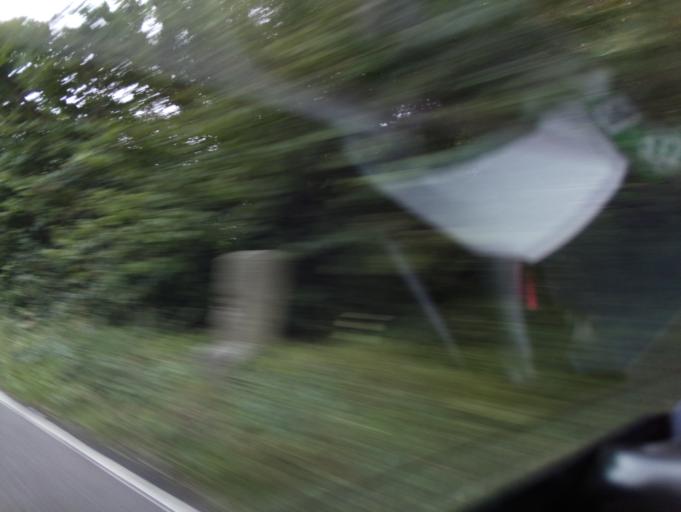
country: GB
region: England
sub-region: Devon
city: Exminster
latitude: 50.6646
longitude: -3.4828
